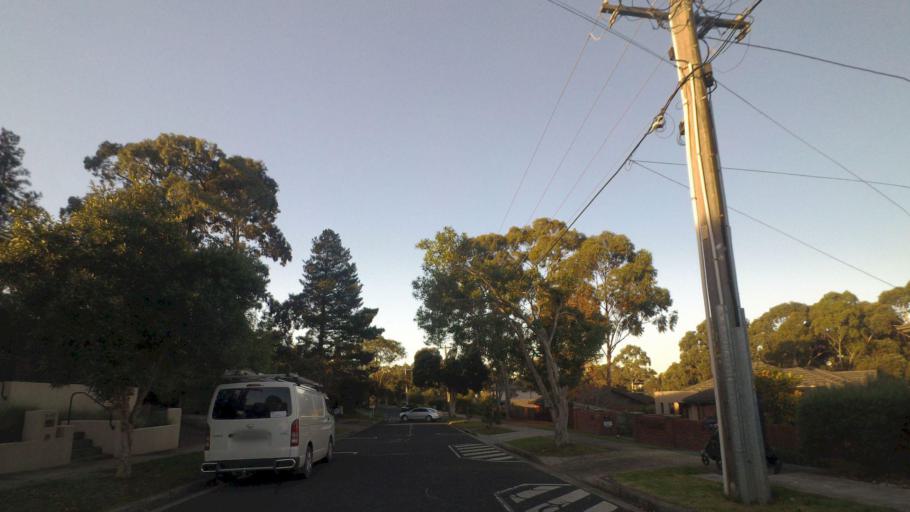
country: AU
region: Victoria
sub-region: Manningham
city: Donvale
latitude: -37.7996
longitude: 145.1652
